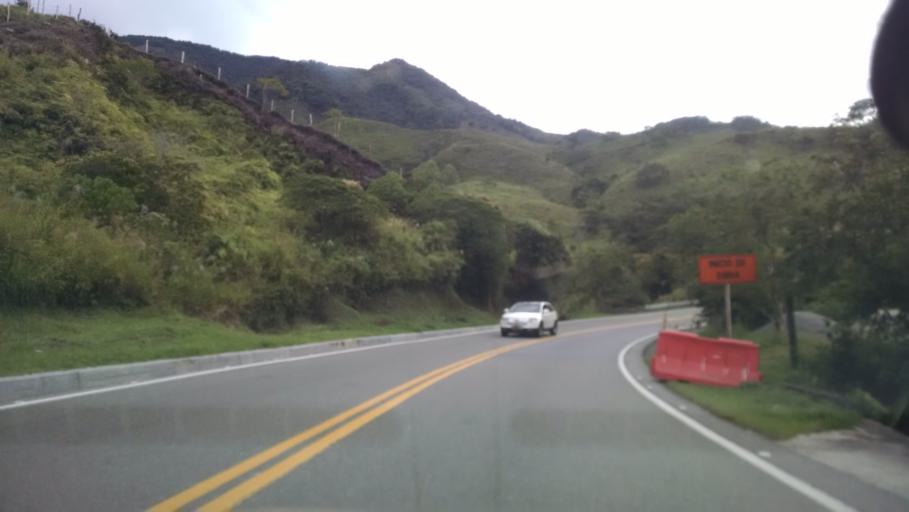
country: CO
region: Antioquia
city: Cocorna
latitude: 6.0276
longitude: -75.1719
